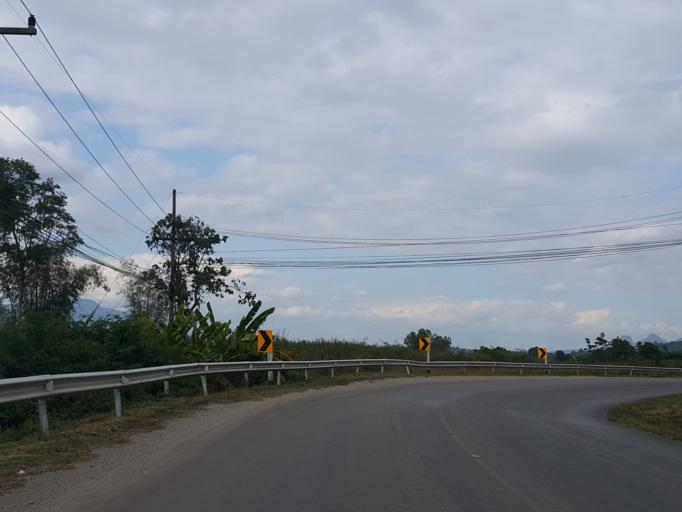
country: TH
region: Lampang
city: Chae Hom
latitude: 18.5898
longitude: 99.4721
